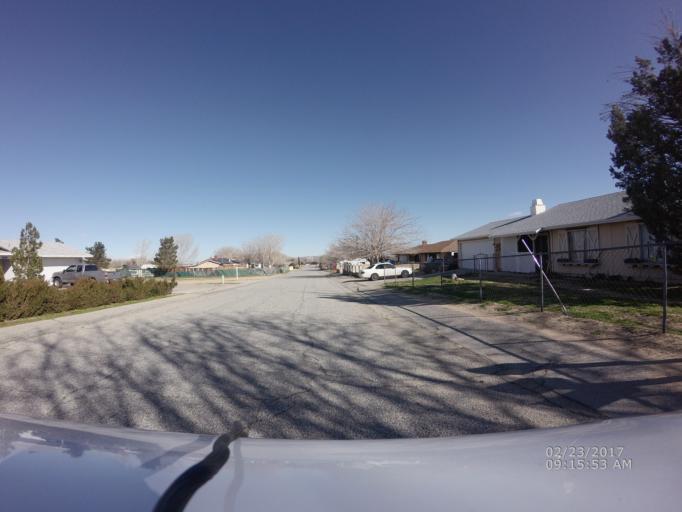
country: US
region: California
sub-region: Los Angeles County
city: Lake Los Angeles
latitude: 34.6128
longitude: -117.8420
